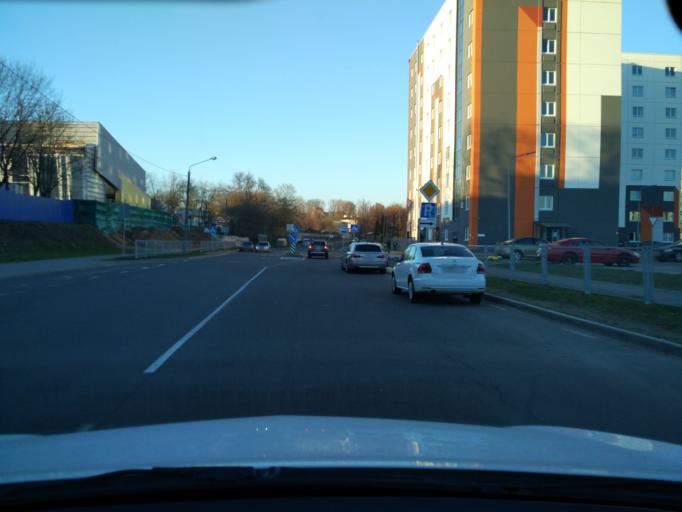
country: BY
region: Minsk
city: Syenitsa
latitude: 53.8668
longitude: 27.5079
